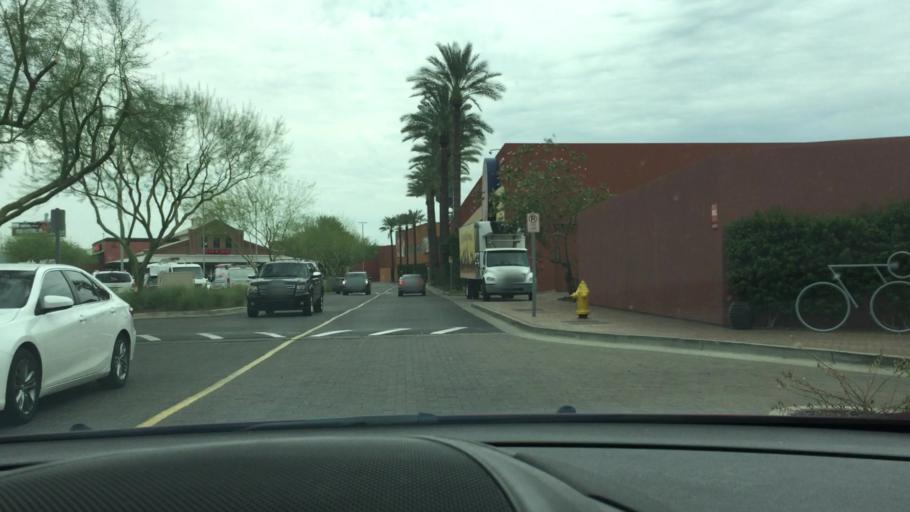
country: US
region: Arizona
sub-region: Maricopa County
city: Tempe
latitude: 33.4333
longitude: -111.9054
